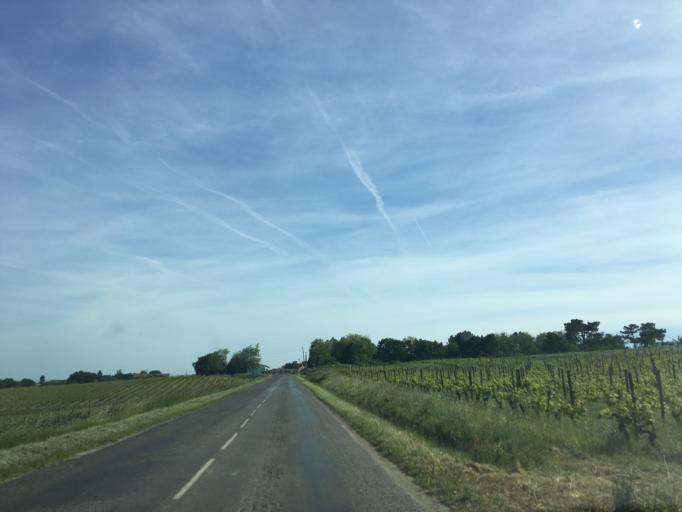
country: FR
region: Poitou-Charentes
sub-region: Departement de la Charente-Maritime
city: Mirambeau
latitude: 45.3332
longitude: -0.5941
